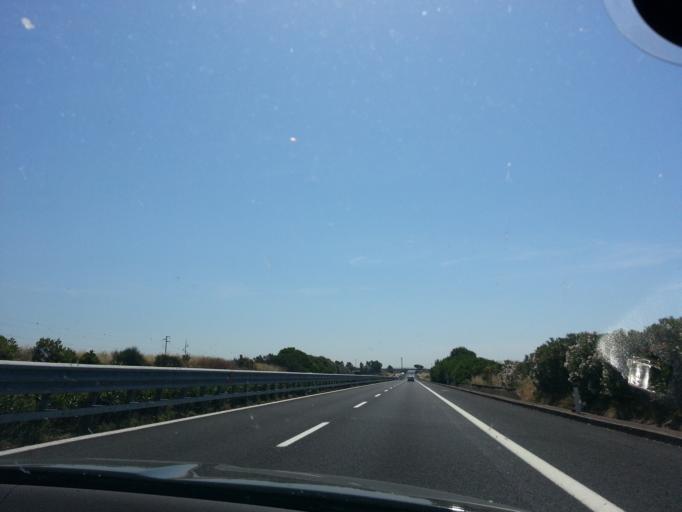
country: IT
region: Latium
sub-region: Citta metropolitana di Roma Capitale
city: Marina di Cerveteri
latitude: 42.0131
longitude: 12.0156
